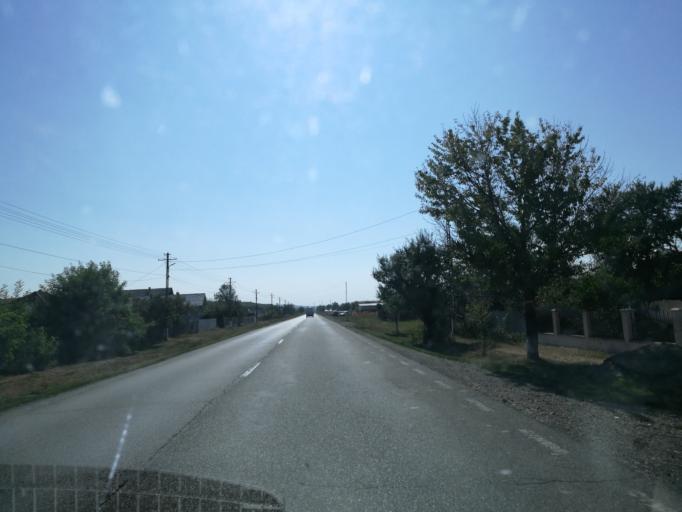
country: RO
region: Iasi
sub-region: Comuna Cristesti
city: Cristesti
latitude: 47.2690
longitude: 26.5267
